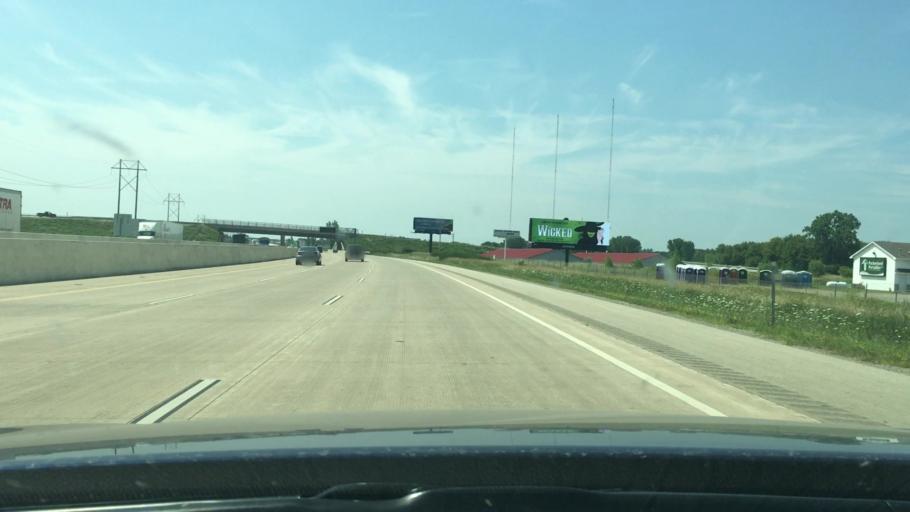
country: US
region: Wisconsin
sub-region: Winnebago County
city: Oshkosh
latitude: 44.0856
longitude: -88.5590
